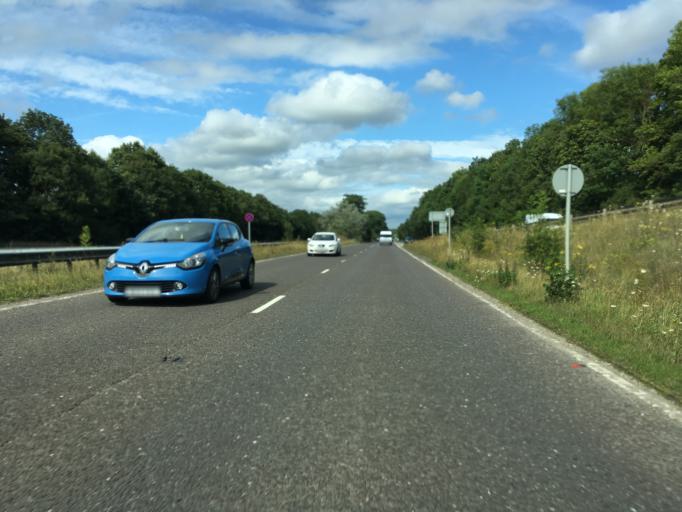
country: GB
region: England
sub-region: West Sussex
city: Horsham
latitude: 51.0713
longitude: -0.3496
